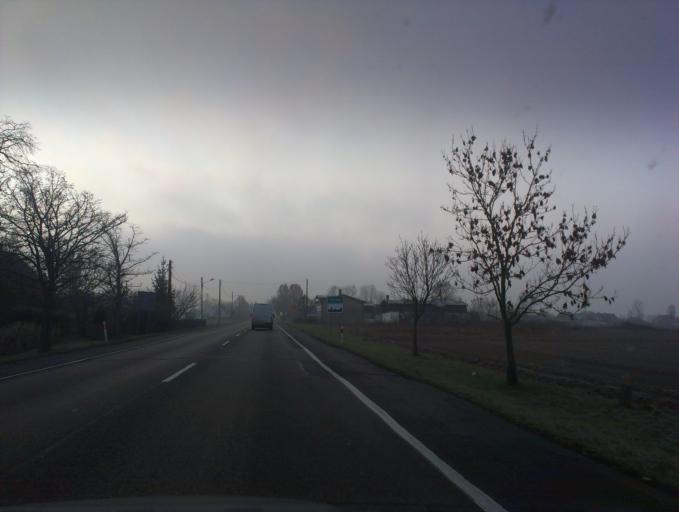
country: PL
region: Greater Poland Voivodeship
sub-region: Powiat chodzieski
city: Budzyn
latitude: 52.8209
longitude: 16.9797
